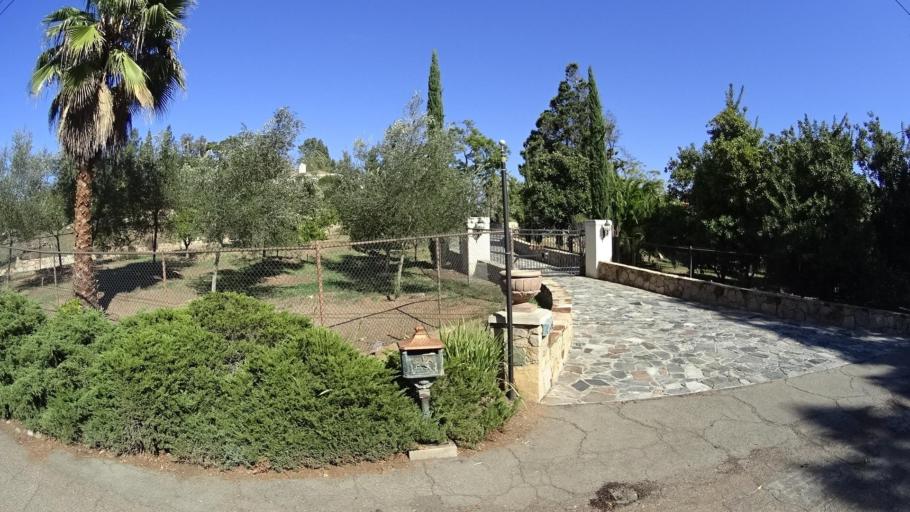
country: US
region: California
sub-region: San Diego County
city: Casa de Oro-Mount Helix
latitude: 32.7653
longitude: -116.9748
